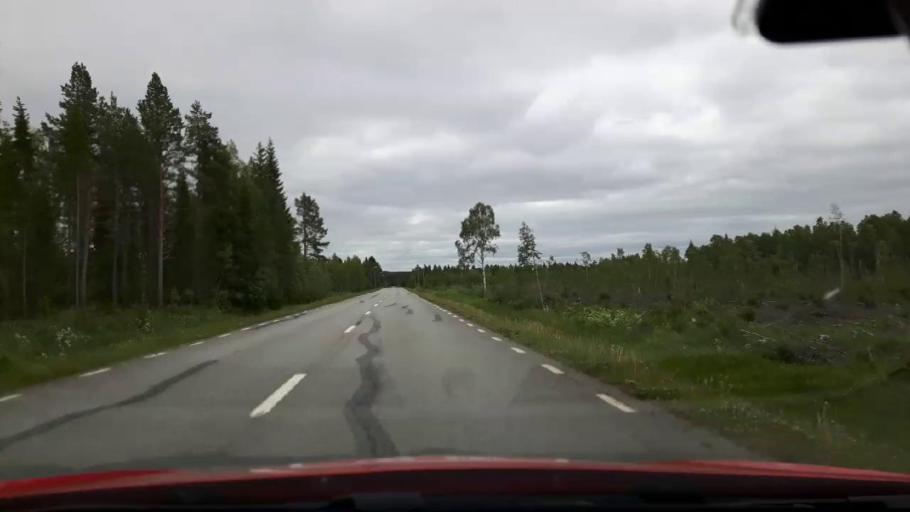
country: SE
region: Jaemtland
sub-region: Stroemsunds Kommun
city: Stroemsund
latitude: 63.5431
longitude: 15.4234
